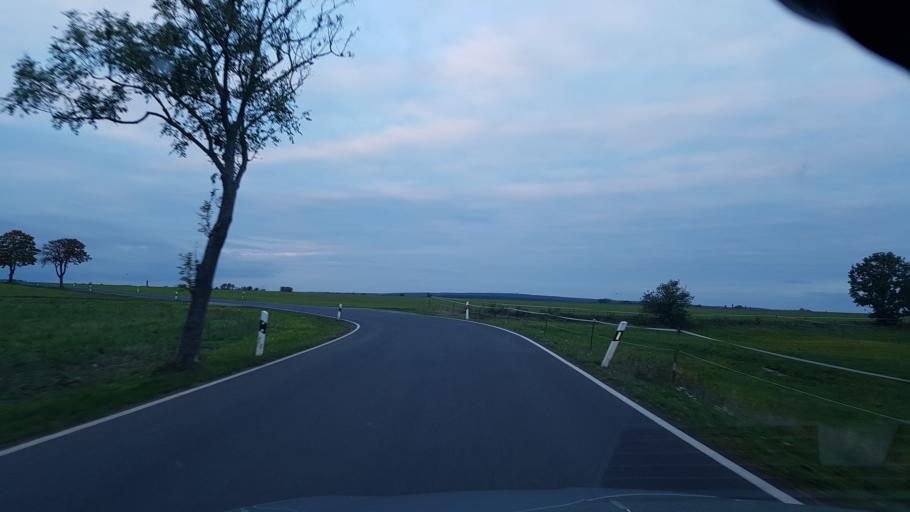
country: DE
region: Saxony
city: Grossenhain
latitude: 51.3222
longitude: 13.5792
